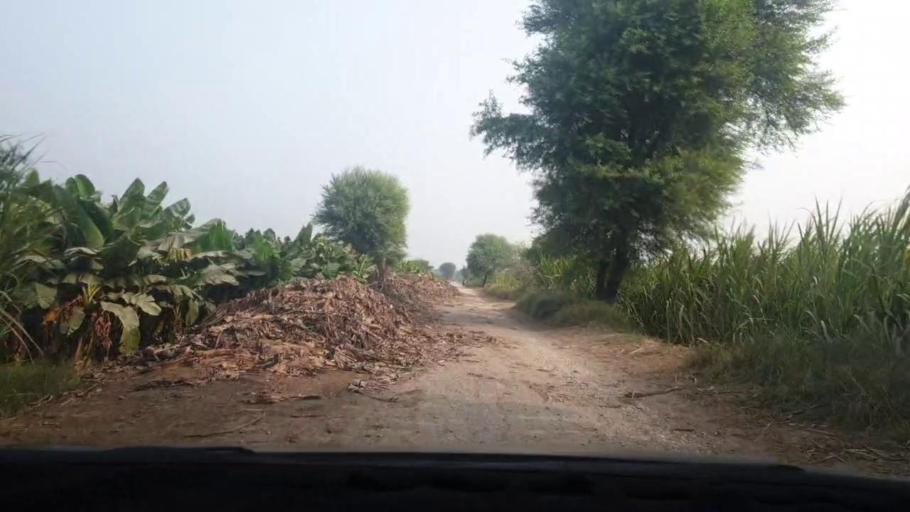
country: PK
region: Sindh
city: Matiari
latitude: 25.5775
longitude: 68.5135
